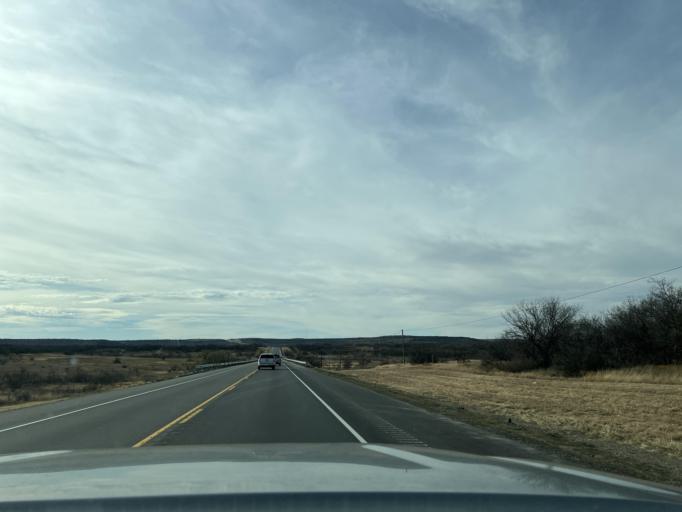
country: US
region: Texas
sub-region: Shackelford County
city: Albany
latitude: 32.7144
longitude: -99.3352
